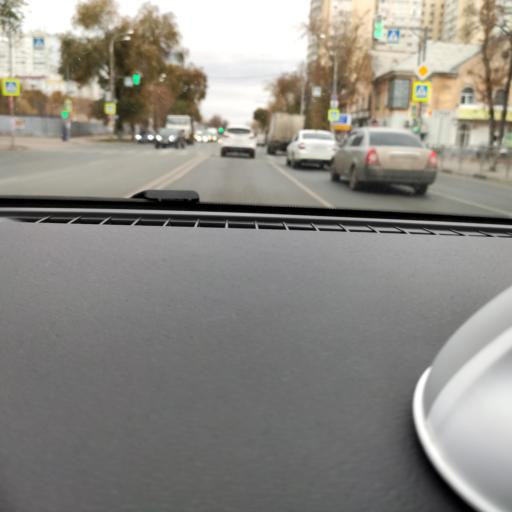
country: RU
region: Samara
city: Samara
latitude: 53.2036
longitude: 50.1899
